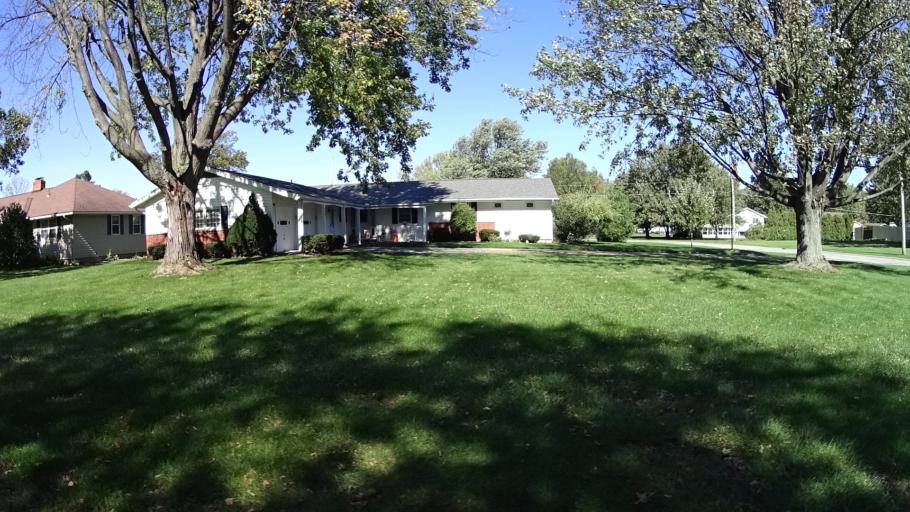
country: US
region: Ohio
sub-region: Lorain County
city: Amherst
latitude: 41.4088
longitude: -82.2217
